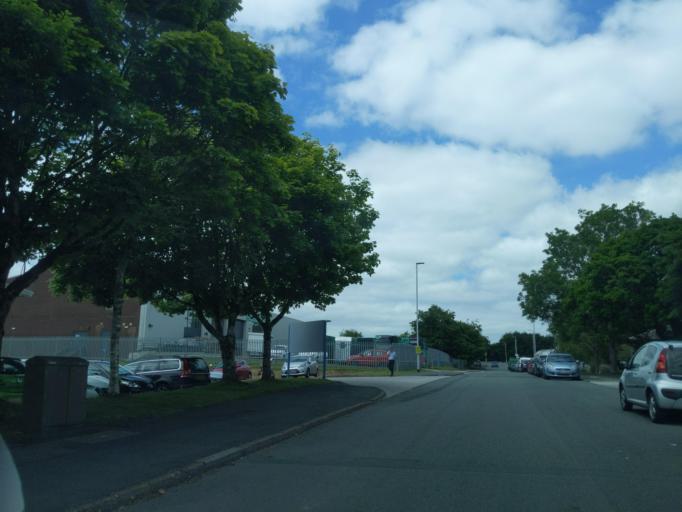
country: GB
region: England
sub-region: Devon
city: Plympton
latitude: 50.4192
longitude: -4.0891
